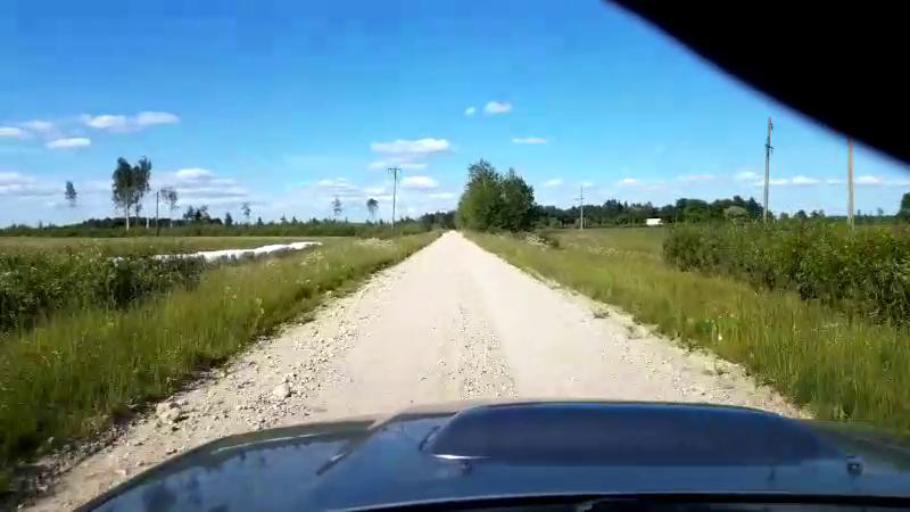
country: EE
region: Paernumaa
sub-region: Sauga vald
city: Sauga
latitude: 58.5000
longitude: 24.5626
